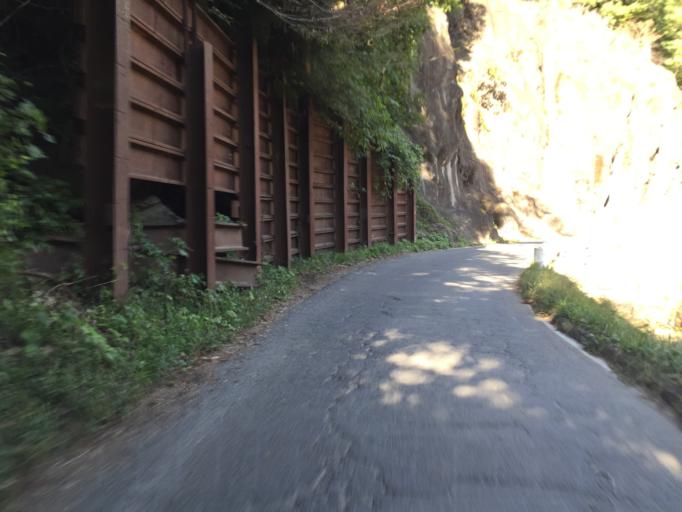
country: JP
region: Miyagi
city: Marumori
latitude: 37.8575
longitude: 140.7532
